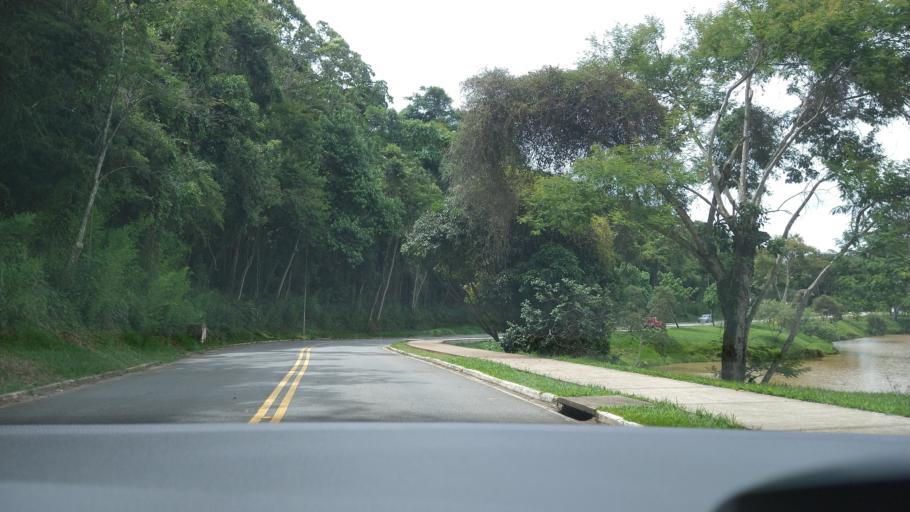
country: BR
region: Minas Gerais
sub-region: Vicosa
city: Vicosa
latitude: -20.7629
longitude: -42.8710
